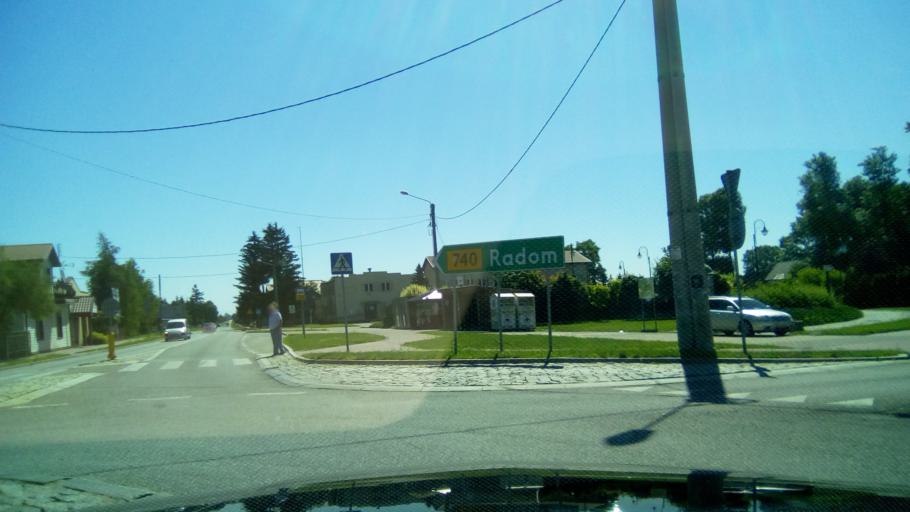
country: PL
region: Masovian Voivodeship
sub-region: Powiat przysuski
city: Potworow
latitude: 51.5081
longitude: 20.7218
